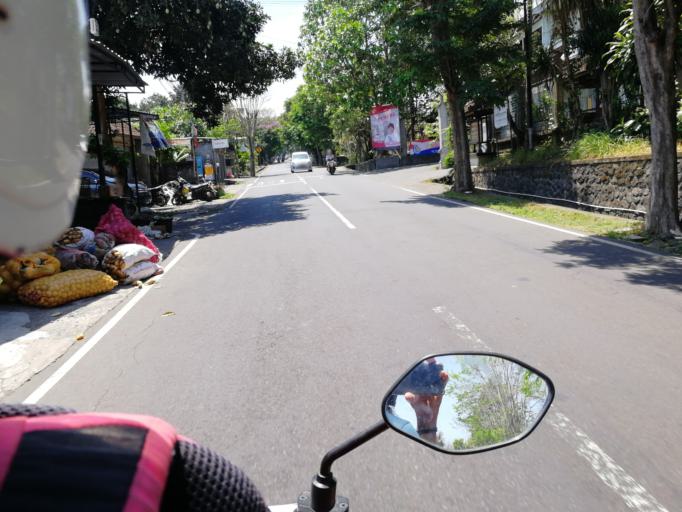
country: ID
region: Bali
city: Banjar Beji
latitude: -8.4480
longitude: 115.5891
